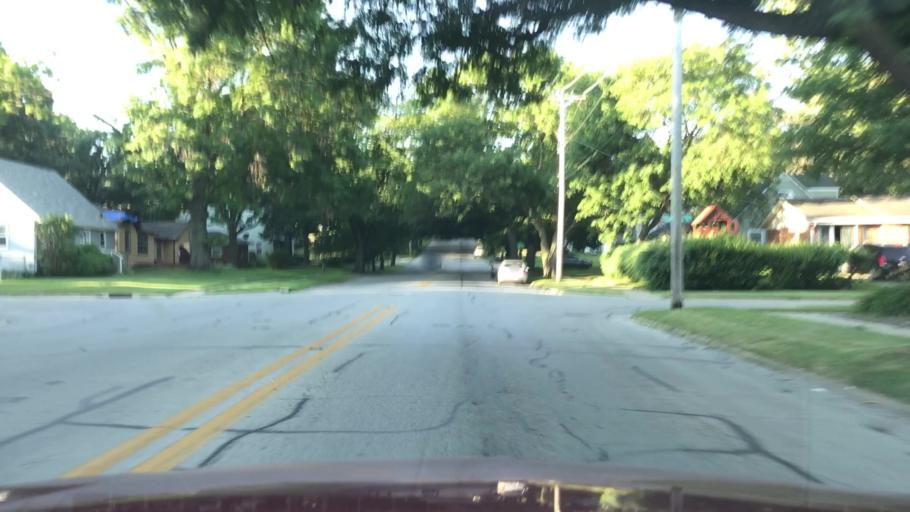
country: US
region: Illinois
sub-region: Winnebago County
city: Rockford
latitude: 42.2651
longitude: -89.0425
